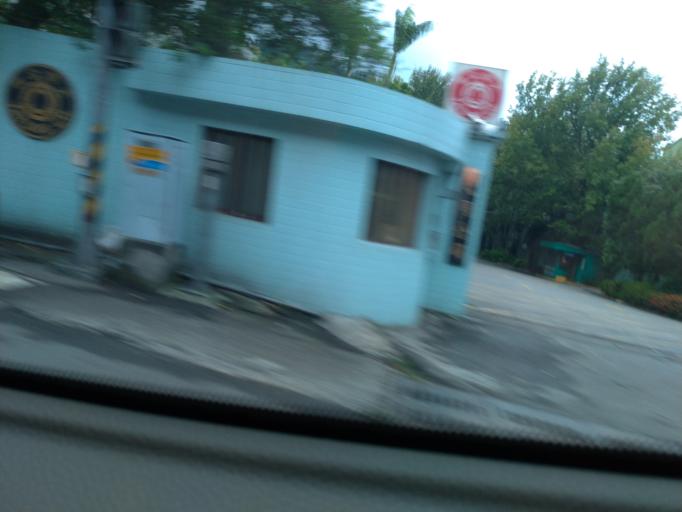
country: TW
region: Taipei
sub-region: Taipei
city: Banqiao
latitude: 24.9288
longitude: 121.4122
